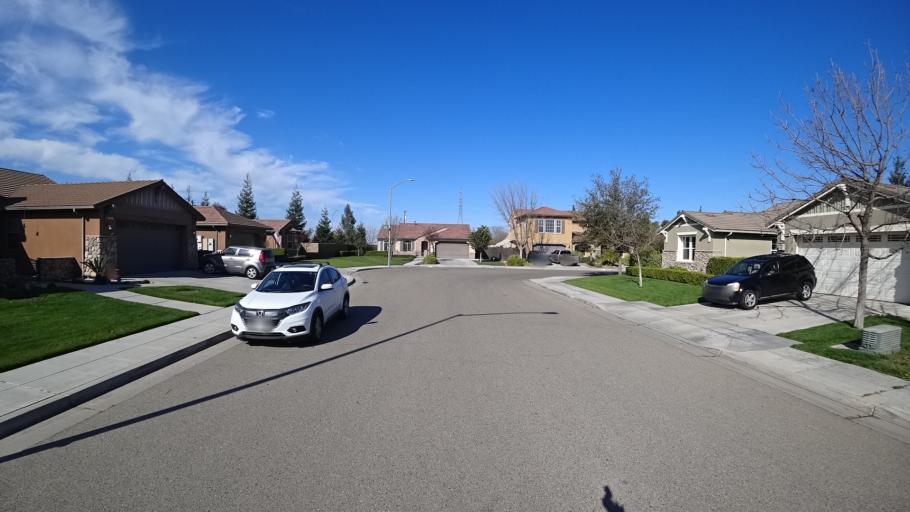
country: US
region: California
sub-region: Fresno County
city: West Park
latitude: 36.7979
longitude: -119.8974
